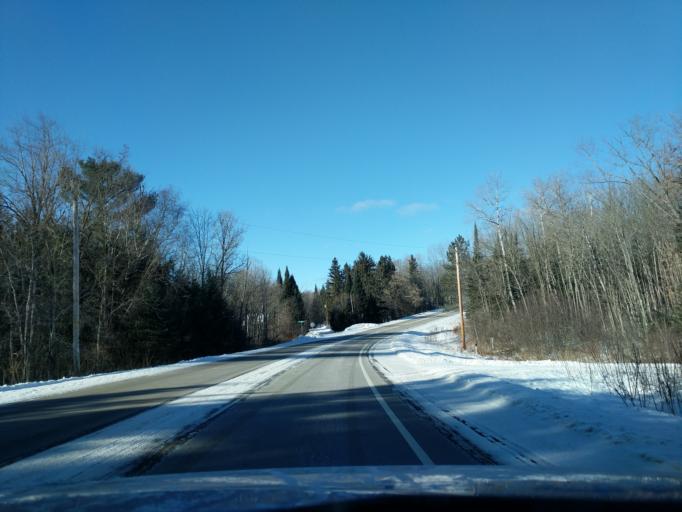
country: US
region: Wisconsin
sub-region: Menominee County
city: Keshena
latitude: 45.1192
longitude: -88.6622
